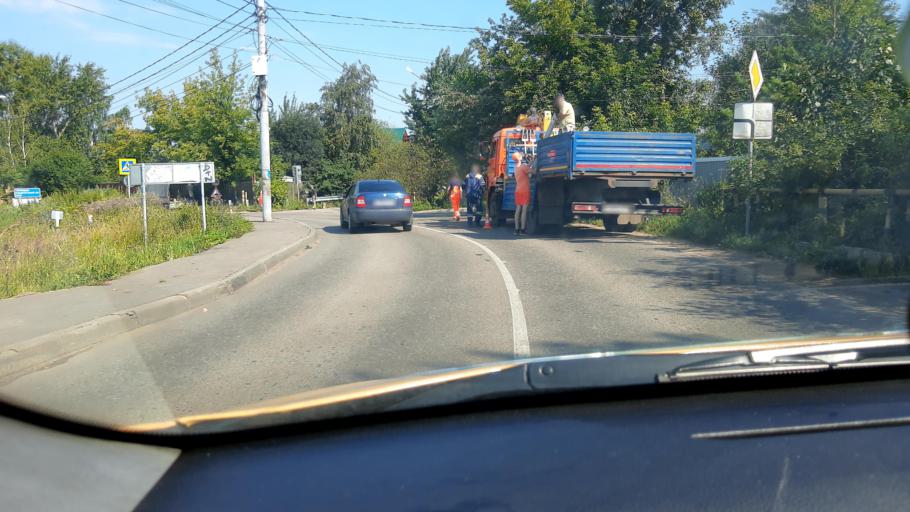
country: RU
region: Moscow
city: Zagor'ye
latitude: 55.5624
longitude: 37.6643
